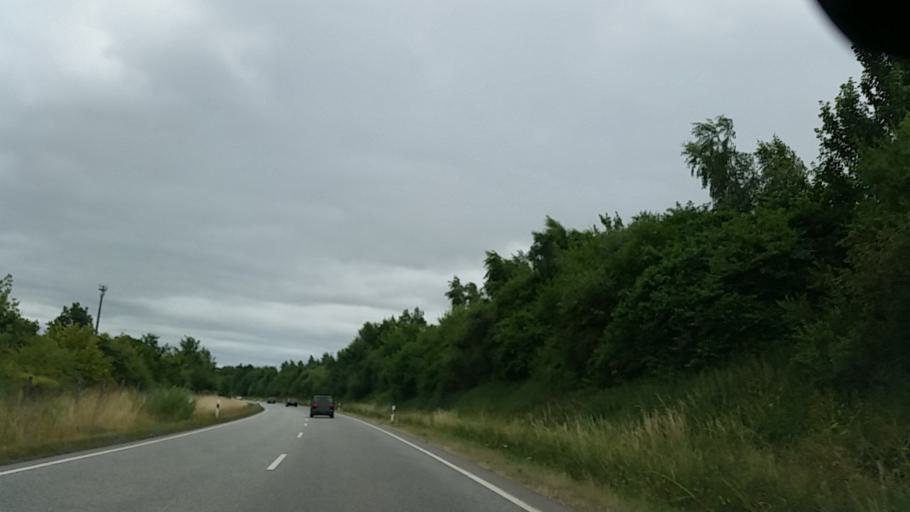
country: DE
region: Schleswig-Holstein
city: Gettorf
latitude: 54.4177
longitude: 9.9767
